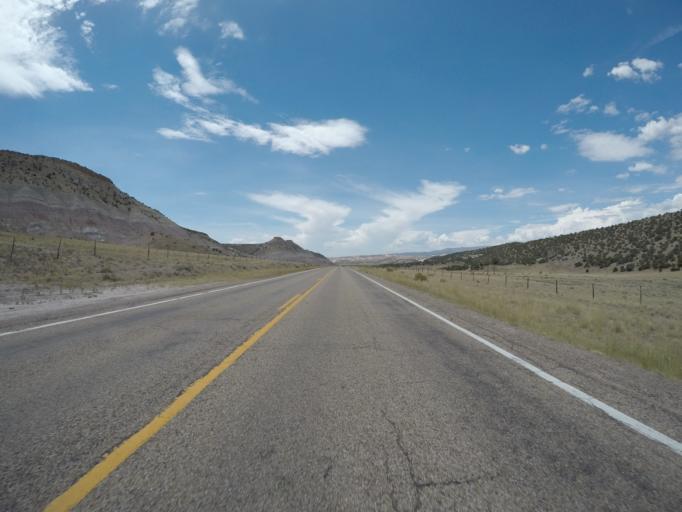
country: US
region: Utah
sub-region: Uintah County
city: Vernal
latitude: 40.5660
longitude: -109.5009
